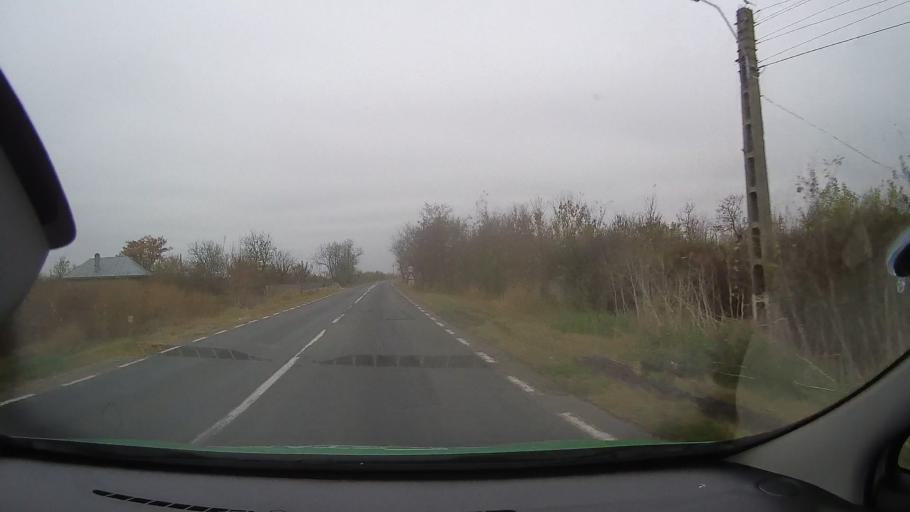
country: RO
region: Braila
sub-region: Comuna Baraganul
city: Baraganul
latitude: 44.7984
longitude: 27.5128
